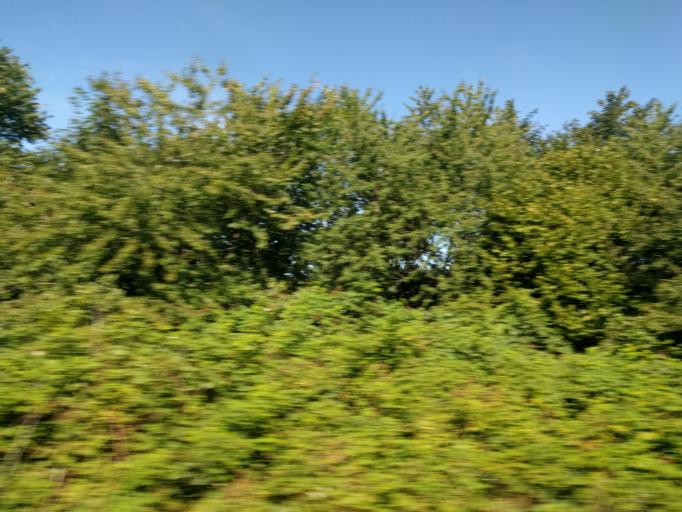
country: DK
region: South Denmark
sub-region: Nyborg Kommune
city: Ullerslev
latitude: 55.3418
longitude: 10.7194
